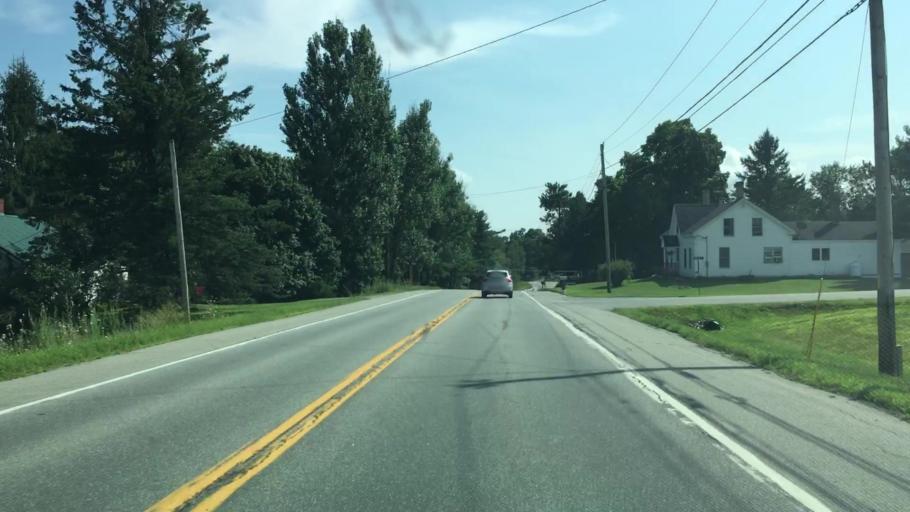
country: US
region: Maine
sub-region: Penobscot County
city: Orrington
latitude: 44.7147
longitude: -68.8463
